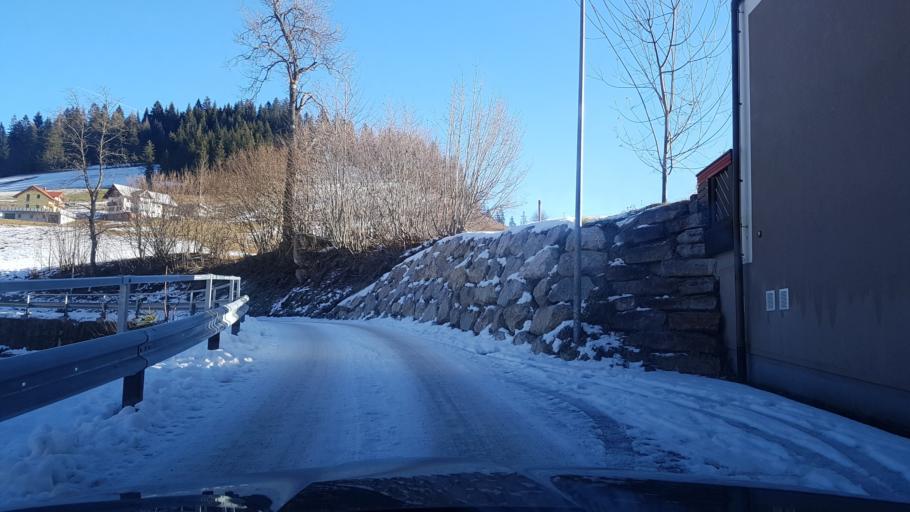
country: AT
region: Salzburg
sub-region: Politischer Bezirk Salzburg-Umgebung
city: Strobl
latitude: 47.5933
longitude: 13.4684
